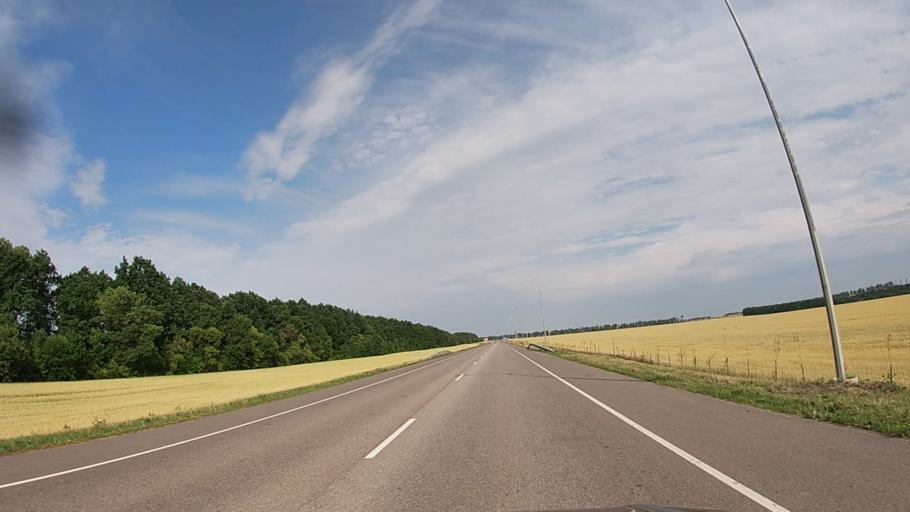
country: RU
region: Belgorod
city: Proletarskiy
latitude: 50.8260
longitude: 35.7793
